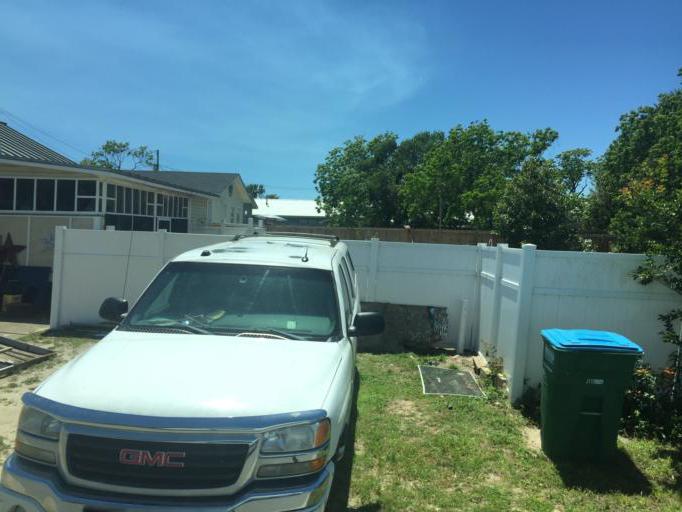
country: US
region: Florida
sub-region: Bay County
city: Laguna Beach
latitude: 30.2430
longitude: -85.9268
